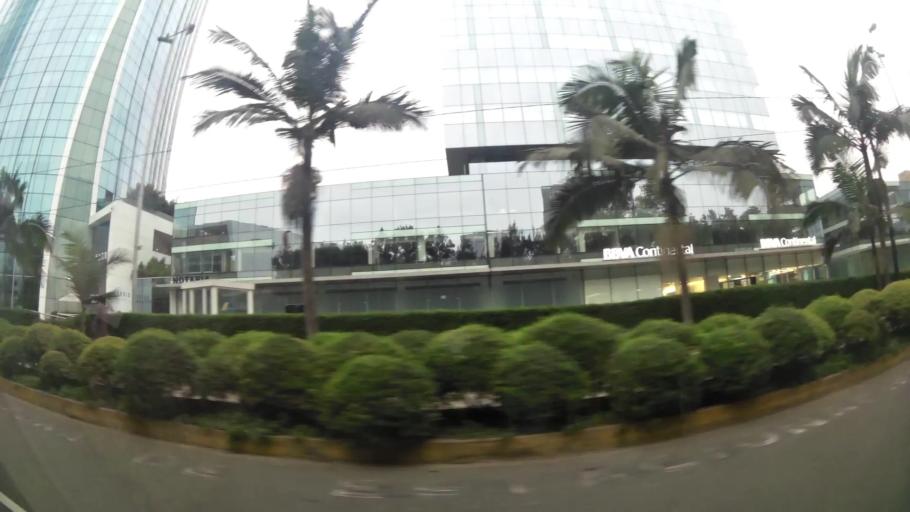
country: PE
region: Lima
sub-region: Lima
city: San Luis
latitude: -12.0929
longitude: -77.0245
